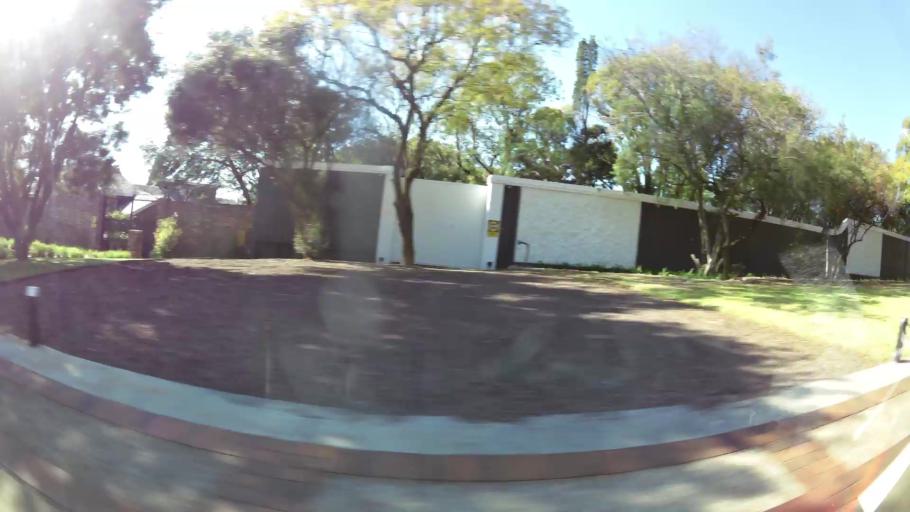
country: ZA
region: Gauteng
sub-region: City of Johannesburg Metropolitan Municipality
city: Midrand
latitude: -26.0531
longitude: 28.0334
